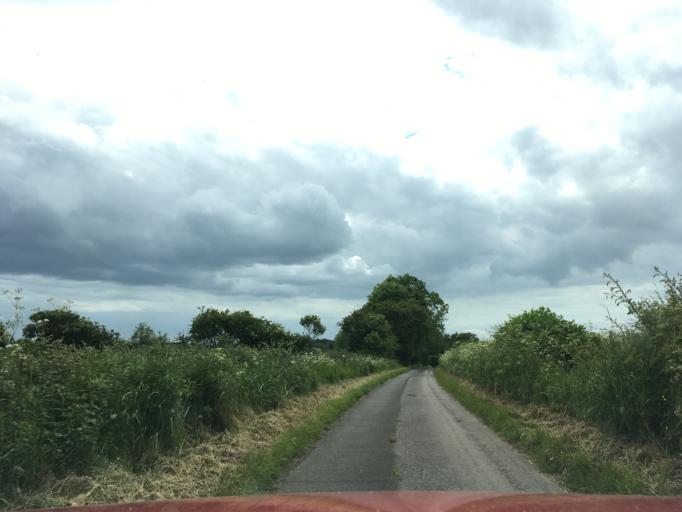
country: GB
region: England
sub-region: Gloucestershire
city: Cirencester
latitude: 51.7630
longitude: -1.9832
